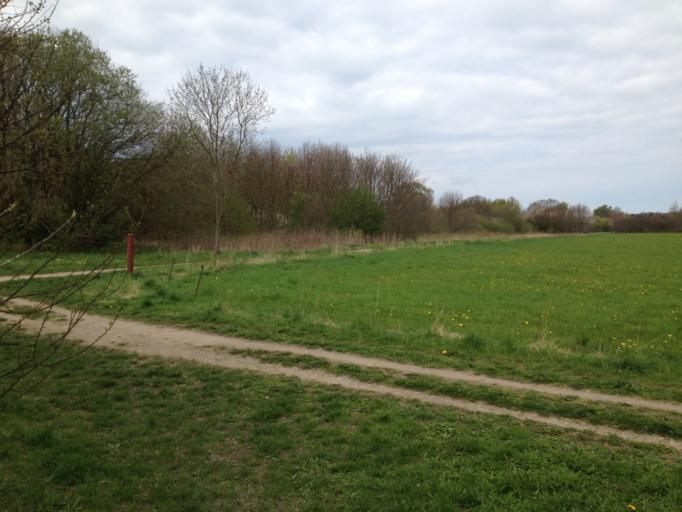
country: DK
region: Capital Region
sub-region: Fredensborg Kommune
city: Niva
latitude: 55.9465
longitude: 12.5096
